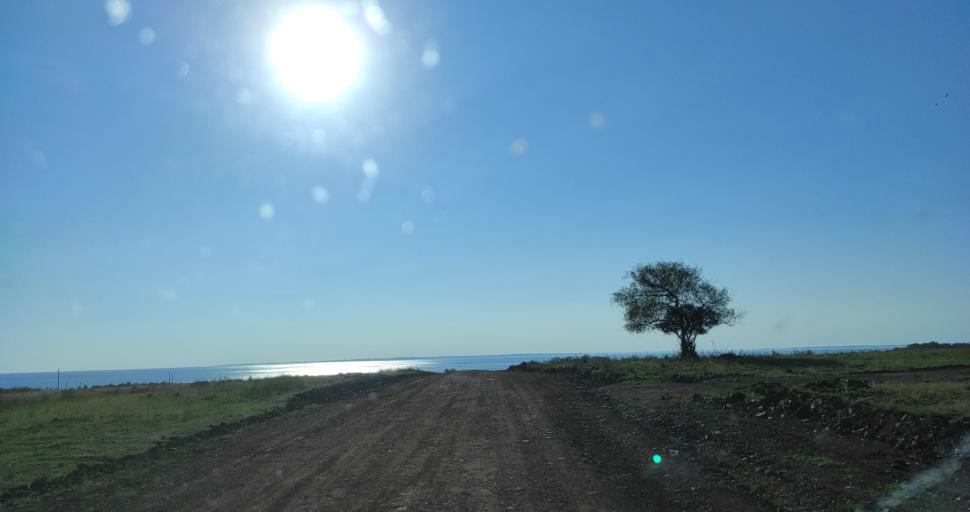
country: PY
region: Itapua
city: Carmen del Parana
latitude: -27.4105
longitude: -56.1768
